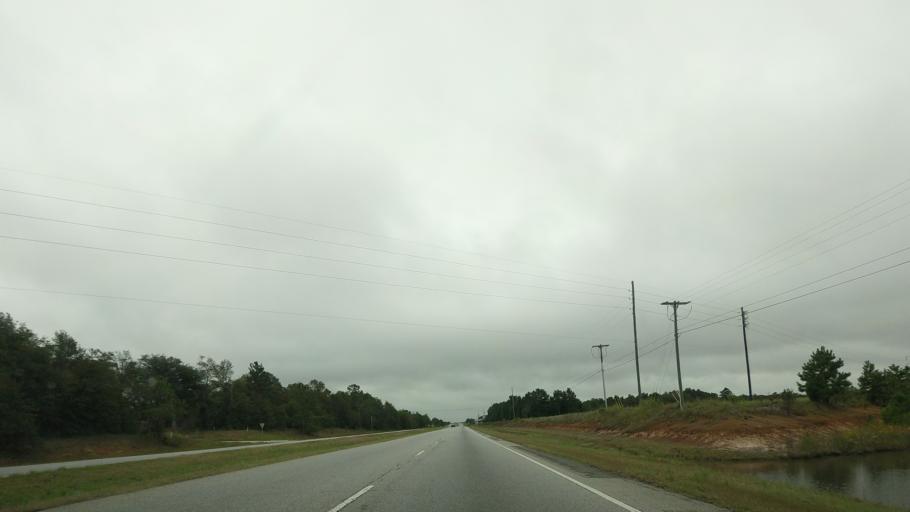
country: US
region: Georgia
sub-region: Lowndes County
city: Valdosta
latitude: 30.8412
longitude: -83.2280
